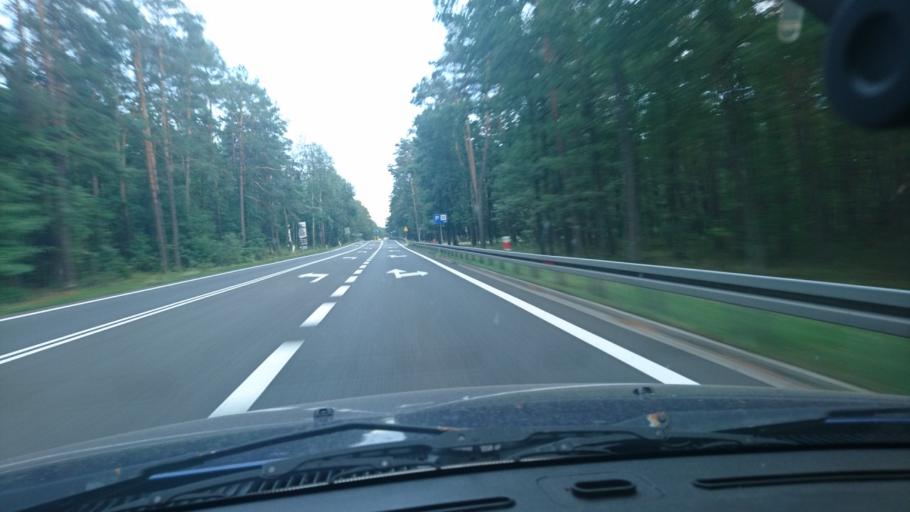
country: PL
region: Silesian Voivodeship
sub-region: Powiat lubliniecki
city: Lubliniec
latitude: 50.6116
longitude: 18.6933
